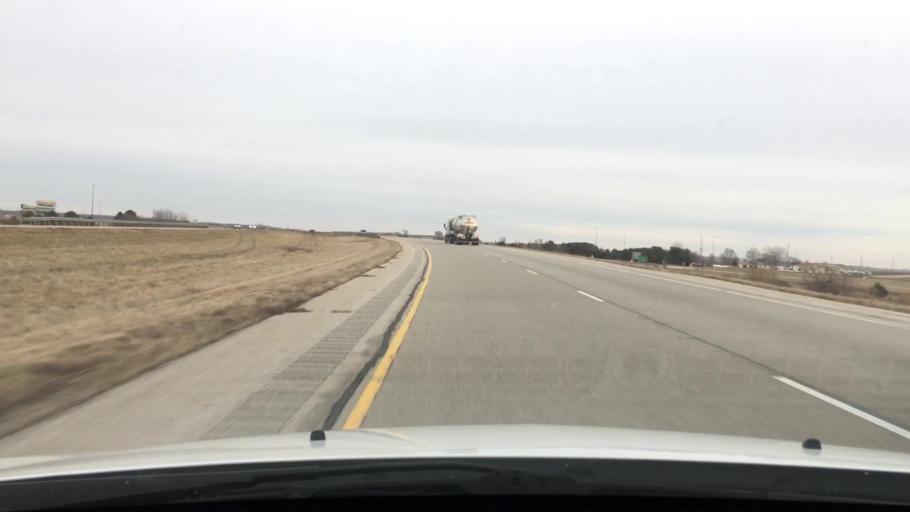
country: US
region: Illinois
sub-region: Logan County
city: Atlanta
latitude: 40.3101
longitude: -89.1649
